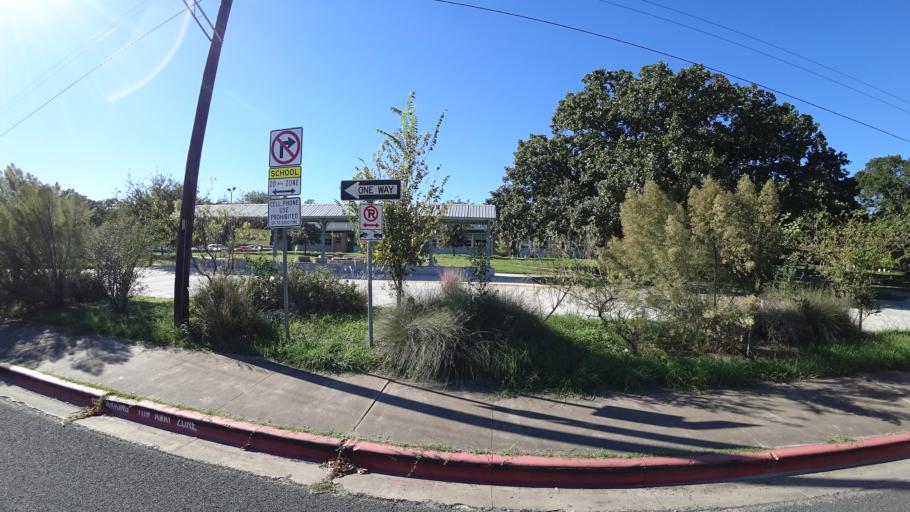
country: US
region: Texas
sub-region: Travis County
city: West Lake Hills
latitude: 30.3298
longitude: -97.7596
